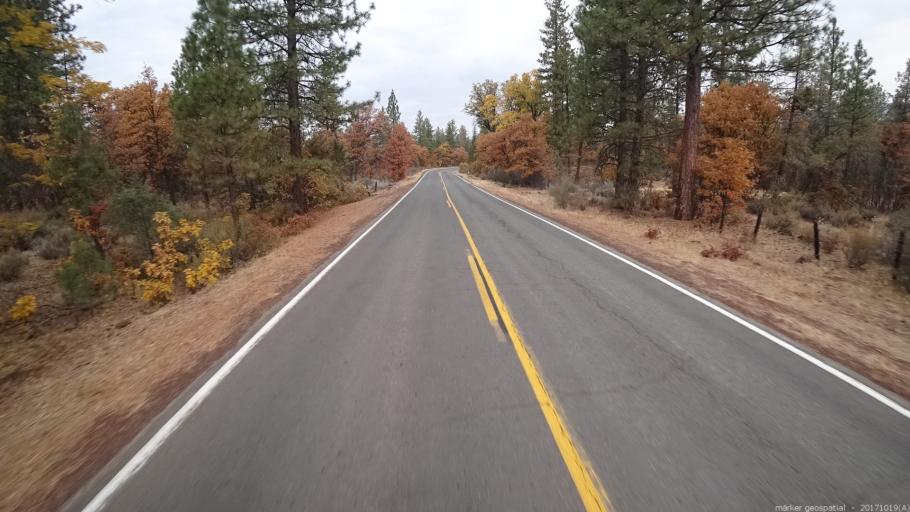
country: US
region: California
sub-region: Shasta County
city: Burney
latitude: 41.1128
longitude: -121.3314
